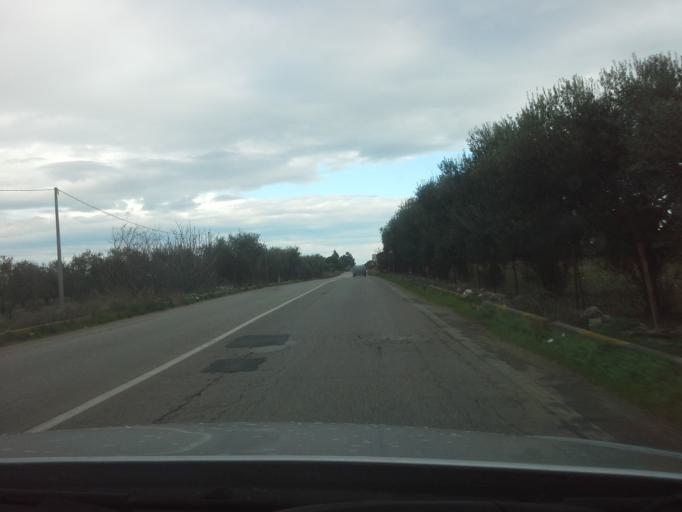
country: IT
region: Apulia
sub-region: Provincia di Bari
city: Adelfia
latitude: 41.0031
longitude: 16.8991
